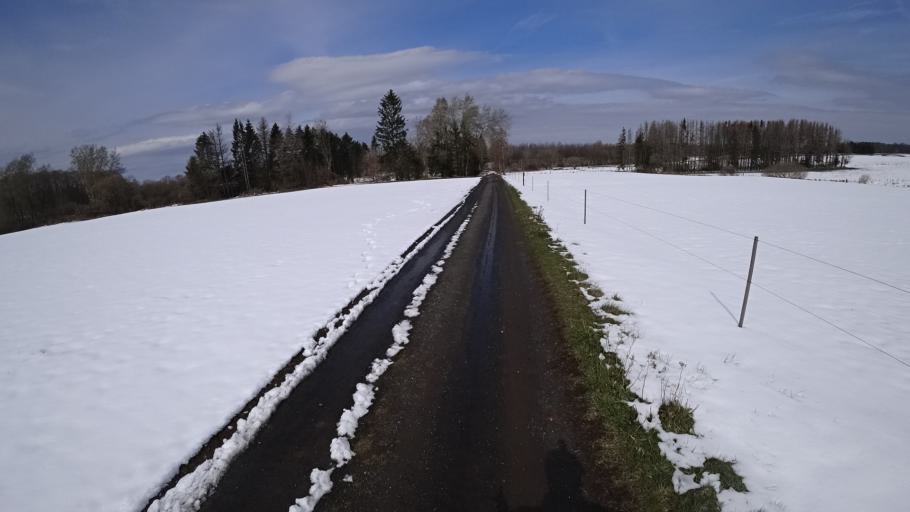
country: DE
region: Rheinland-Pfalz
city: Kausen
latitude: 50.7207
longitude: 7.8724
